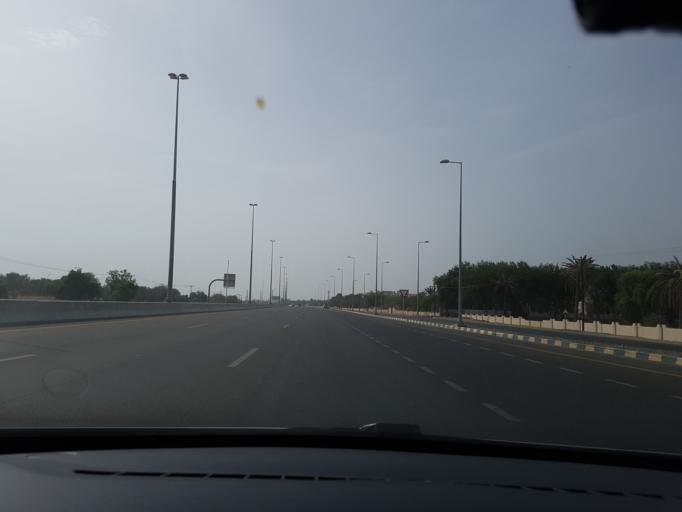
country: OM
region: Al Batinah
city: Al Sohar
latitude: 24.3344
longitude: 56.7378
